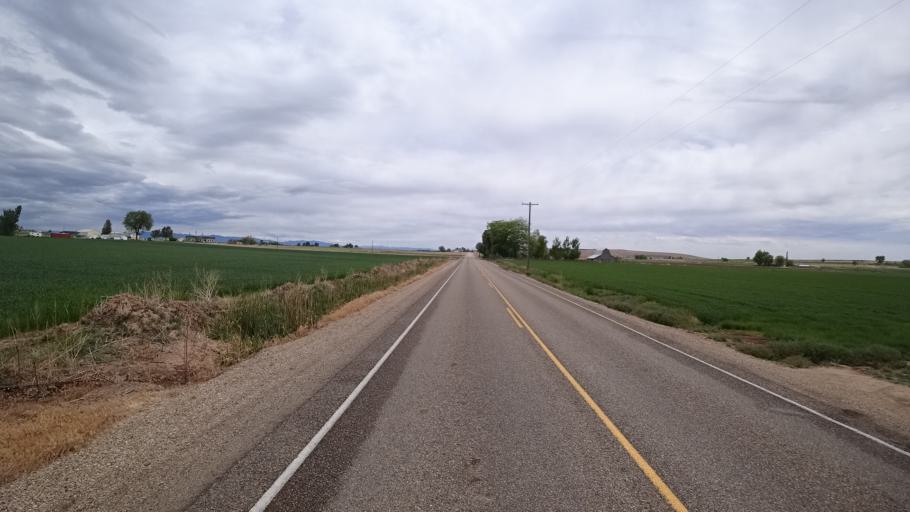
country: US
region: Idaho
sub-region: Canyon County
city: Nampa
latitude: 43.4593
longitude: -116.5165
